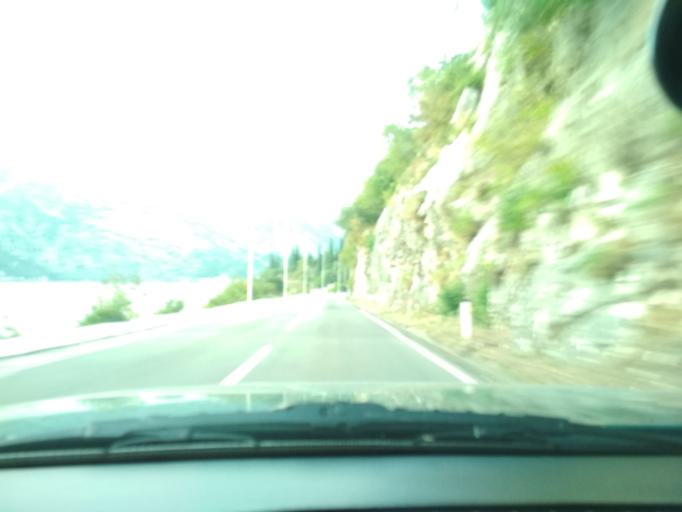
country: ME
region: Kotor
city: Risan
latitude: 42.4985
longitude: 18.6922
